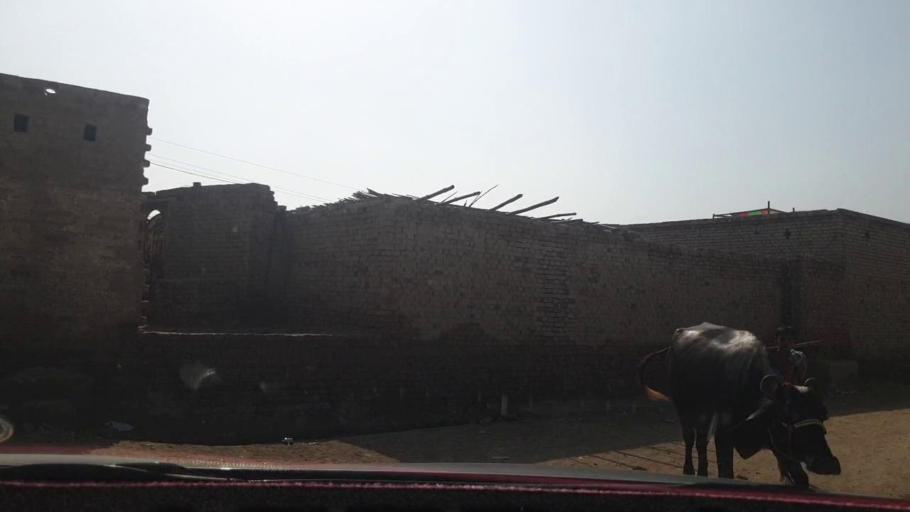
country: PK
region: Sindh
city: Nasirabad
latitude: 27.4382
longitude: 67.9565
